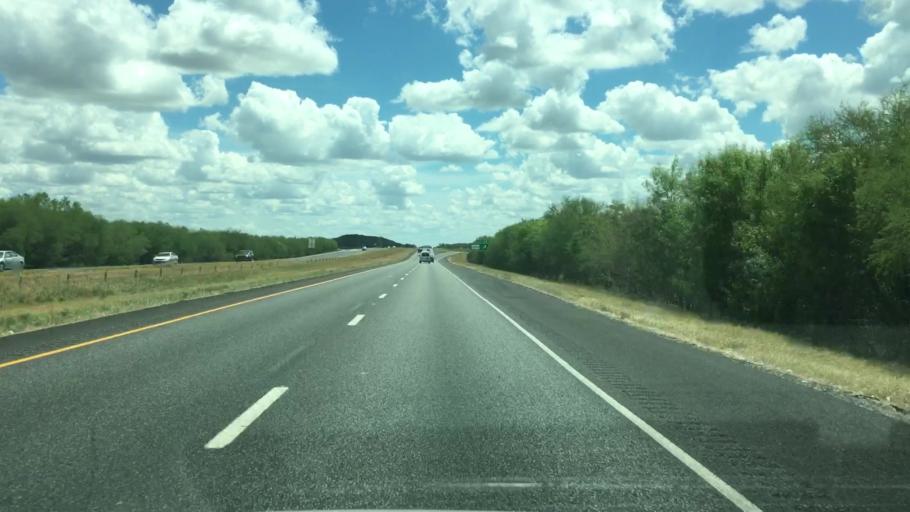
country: US
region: Texas
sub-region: Atascosa County
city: Pleasanton
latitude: 28.7406
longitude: -98.2918
